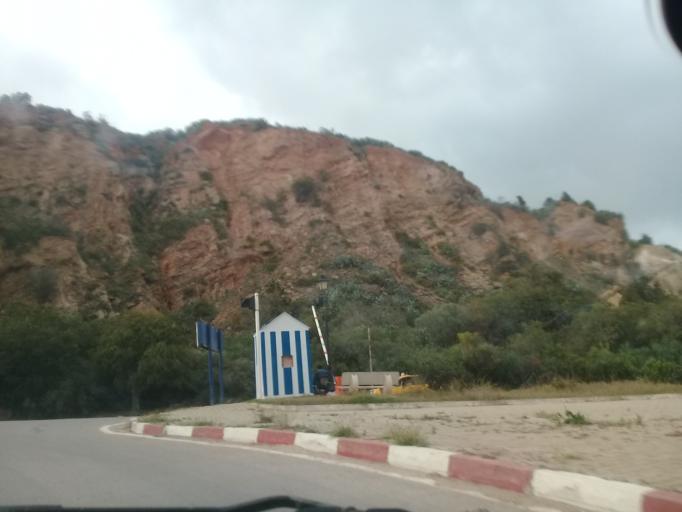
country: TN
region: Tunis
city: Sidi Bou Said
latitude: 36.8650
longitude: 10.3444
